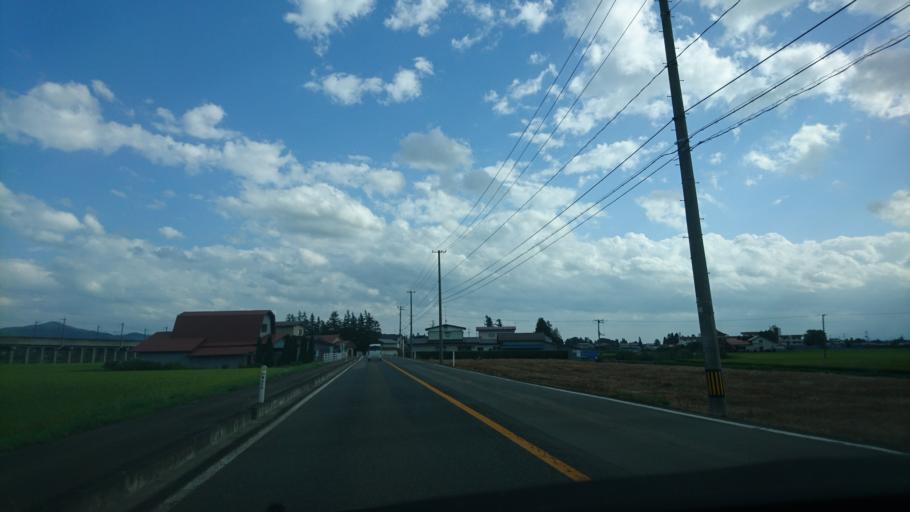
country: JP
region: Iwate
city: Hanamaki
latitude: 39.5022
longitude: 141.1716
